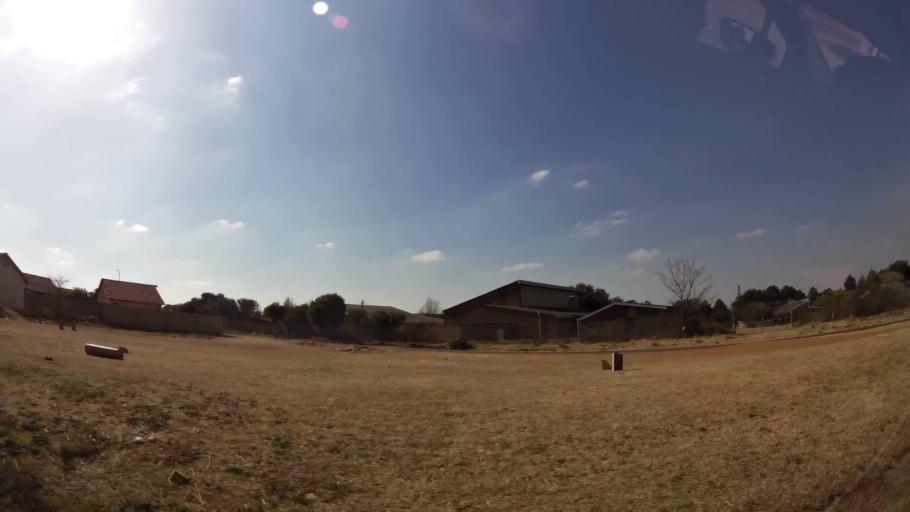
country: ZA
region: Gauteng
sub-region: City of Johannesburg Metropolitan Municipality
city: Roodepoort
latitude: -26.1644
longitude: 27.8009
